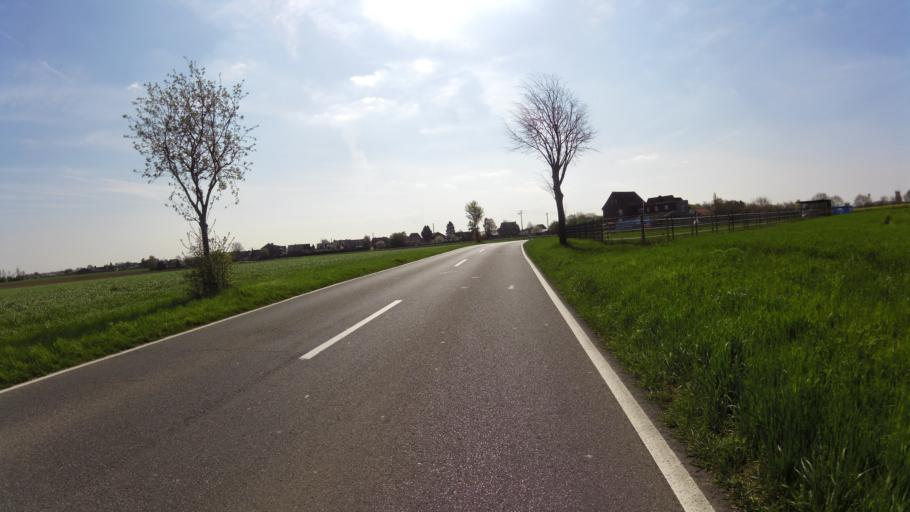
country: DE
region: North Rhine-Westphalia
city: Geilenkirchen
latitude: 50.9862
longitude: 6.0754
